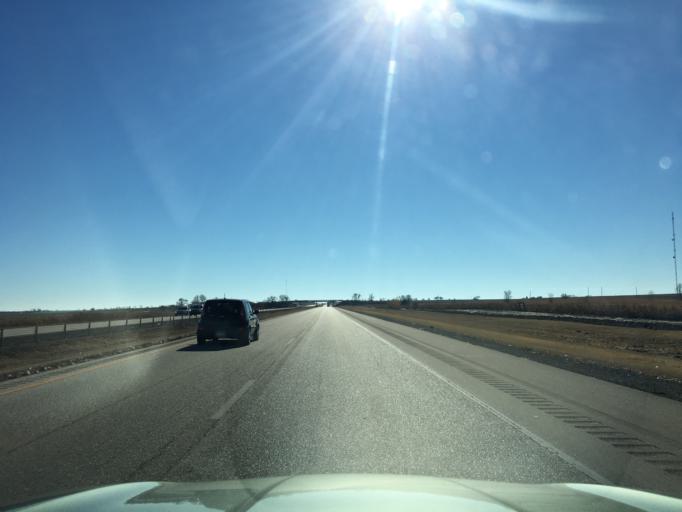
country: US
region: Oklahoma
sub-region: Kay County
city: Blackwell
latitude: 36.8893
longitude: -97.3531
